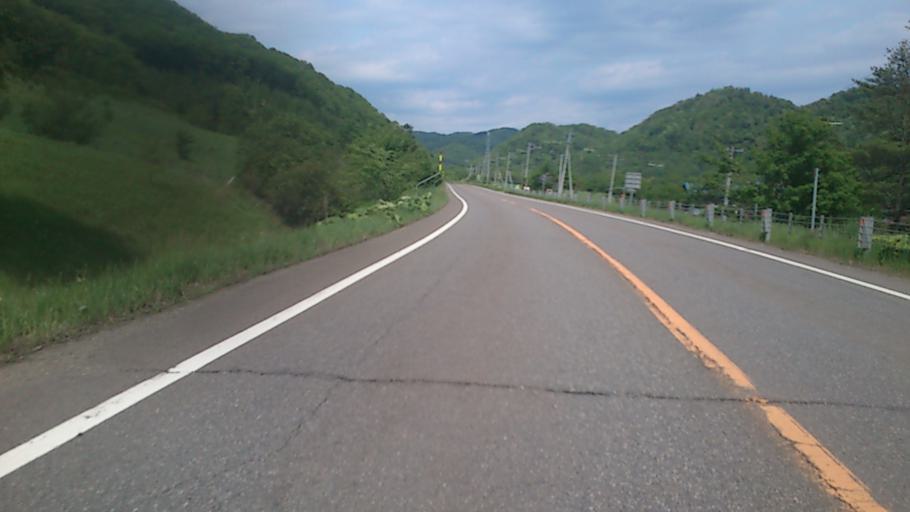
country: JP
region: Hokkaido
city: Kitami
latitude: 43.3438
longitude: 143.7676
